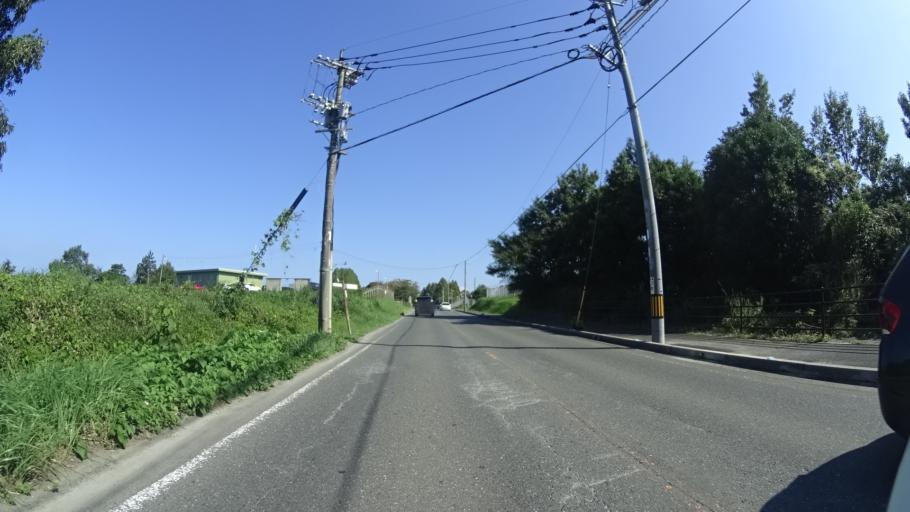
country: JP
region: Fukuoka
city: Tsuiki
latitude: 33.6769
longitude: 131.0071
